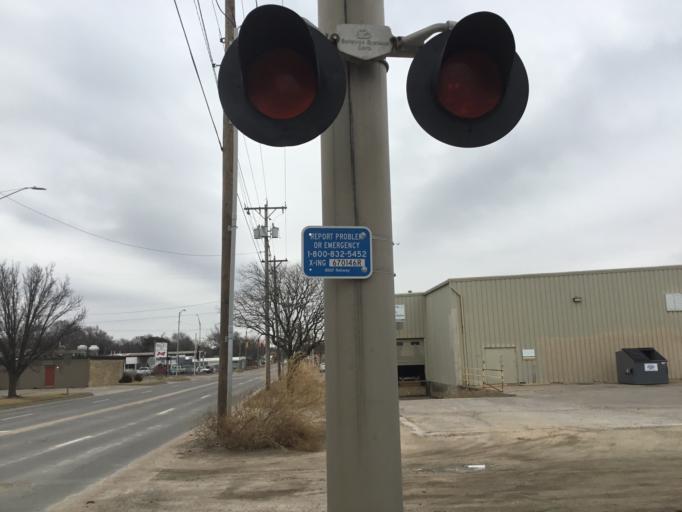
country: US
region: Kansas
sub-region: Sedgwick County
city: Wichita
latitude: 37.6716
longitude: -97.3277
